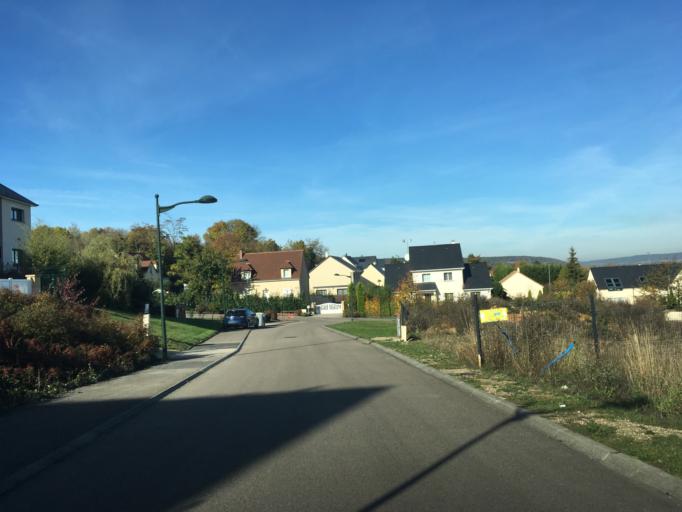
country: FR
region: Haute-Normandie
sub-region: Departement de l'Eure
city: Vernon
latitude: 49.0880
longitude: 1.4573
